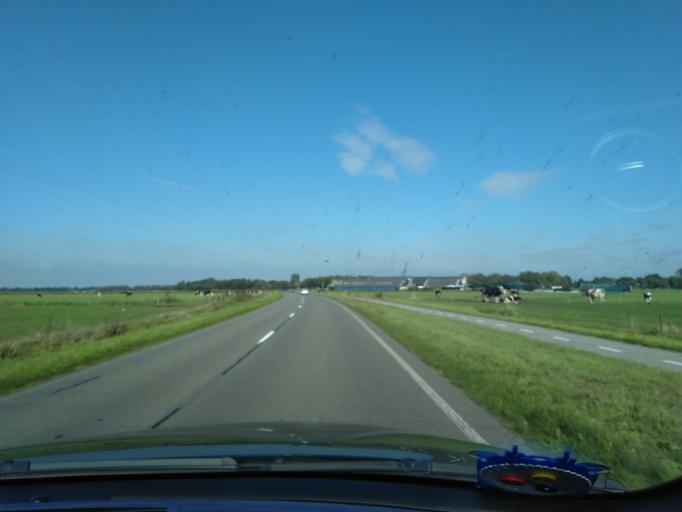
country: NL
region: Drenthe
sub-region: Gemeente Aa en Hunze
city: Anloo
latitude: 53.0677
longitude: 6.7588
